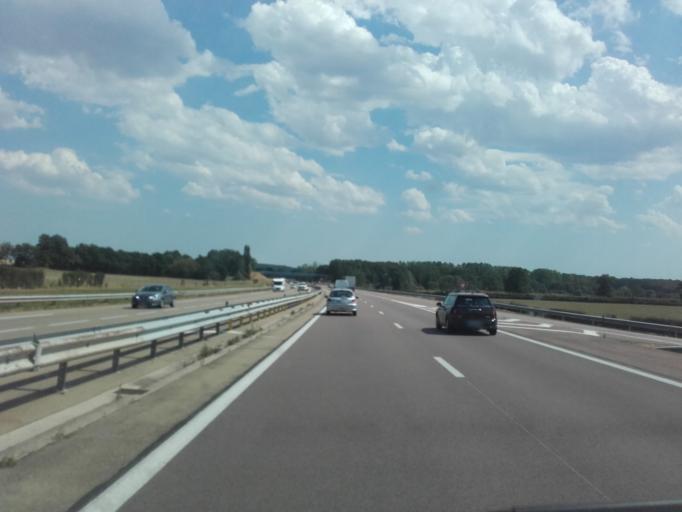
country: FR
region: Bourgogne
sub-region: Departement de l'Yonne
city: Avallon
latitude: 47.5126
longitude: 3.9956
